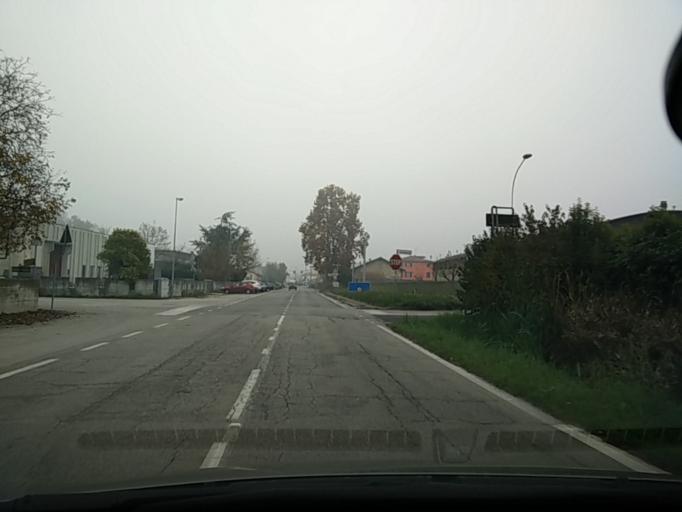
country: IT
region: Veneto
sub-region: Provincia di Venezia
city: Spinea-Orgnano
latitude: 45.5021
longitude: 12.1410
